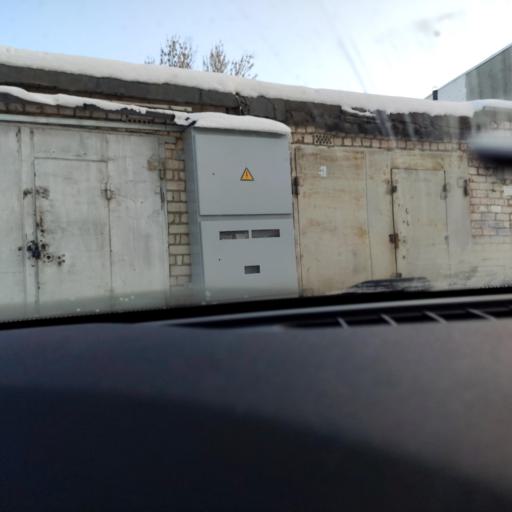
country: RU
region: Samara
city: Smyshlyayevka
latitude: 53.2072
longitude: 50.2874
